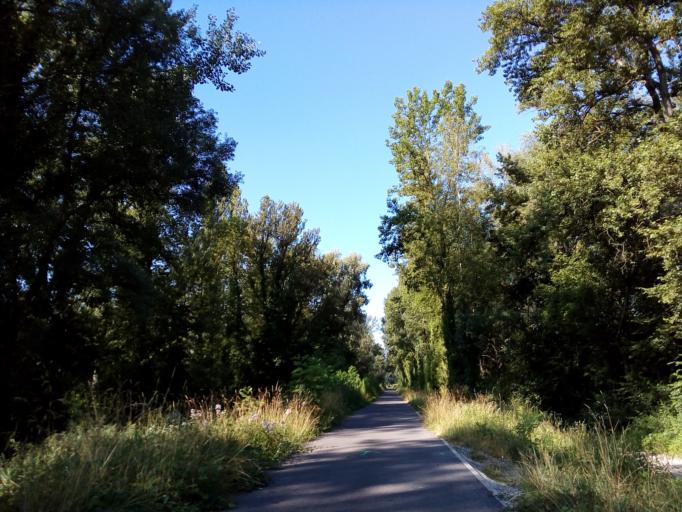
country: FR
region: Rhone-Alpes
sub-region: Departement de l'Isere
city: Le Versoud
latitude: 45.2292
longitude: 5.8518
